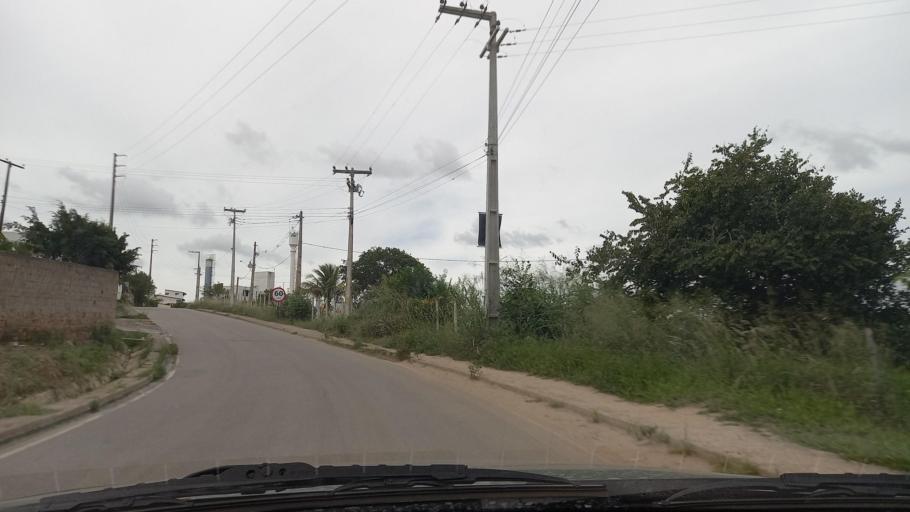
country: BR
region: Pernambuco
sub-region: Gravata
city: Gravata
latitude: -8.2242
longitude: -35.5790
